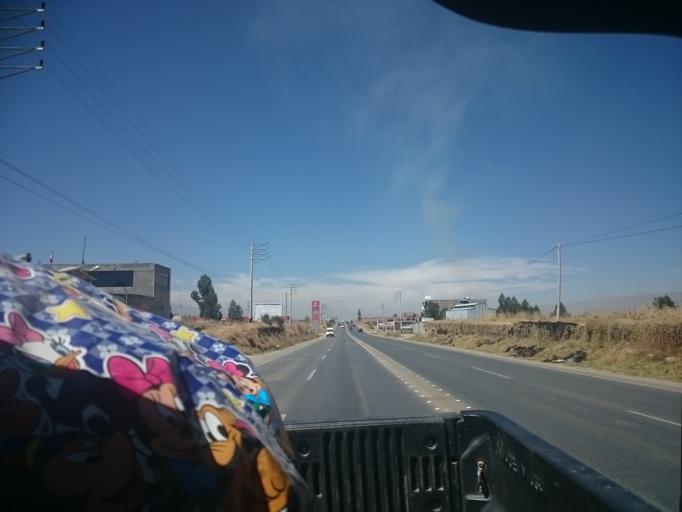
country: PE
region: Junin
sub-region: Provincia de Huancayo
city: San Agustin
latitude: -11.9808
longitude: -75.2632
